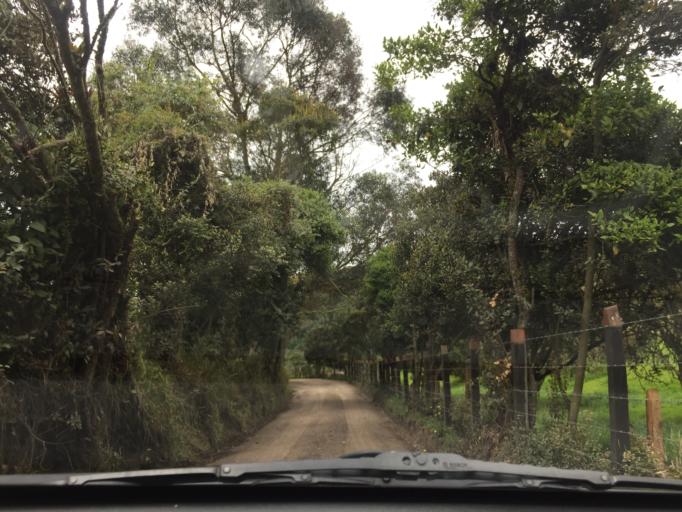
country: CO
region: Cundinamarca
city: Tabio
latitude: 4.9172
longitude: -74.1154
